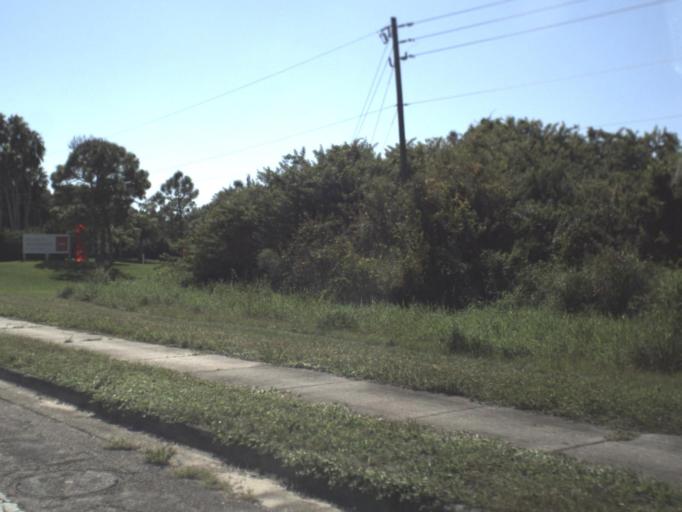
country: US
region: Florida
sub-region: Sarasota County
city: North Port
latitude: 26.9893
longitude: -82.2055
